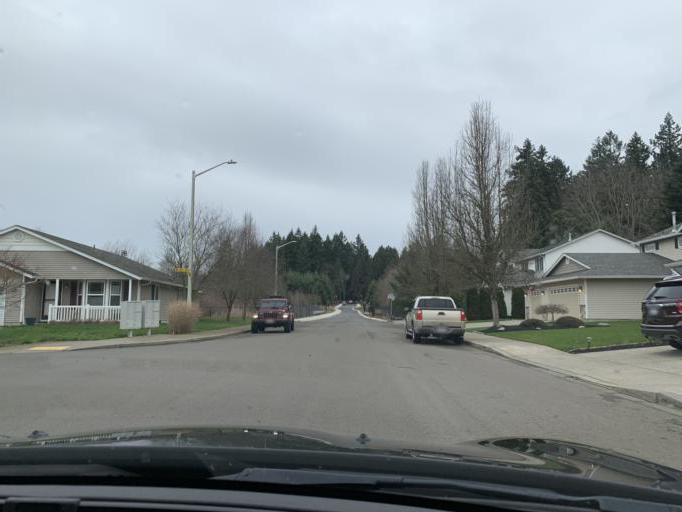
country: US
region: Washington
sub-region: Clark County
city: Five Corners
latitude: 45.6845
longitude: -122.5850
